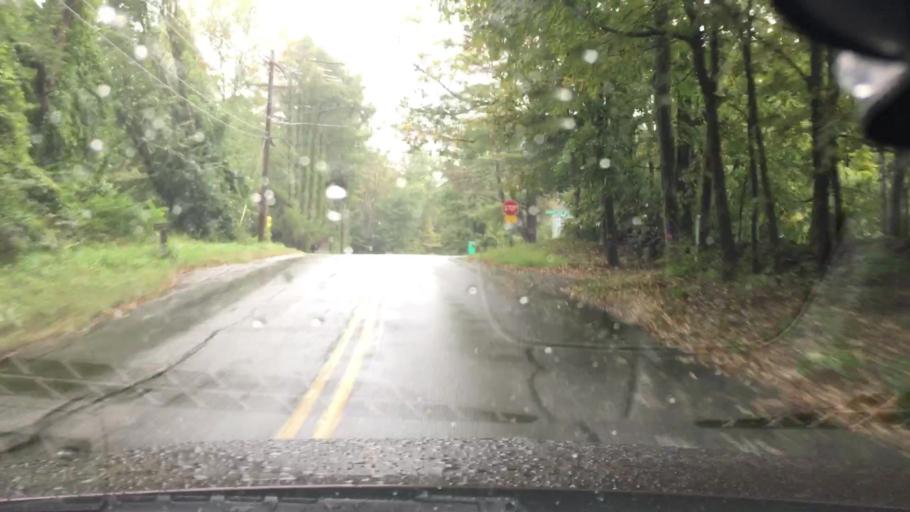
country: US
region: Connecticut
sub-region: Tolland County
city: Storrs
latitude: 41.8167
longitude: -72.2827
